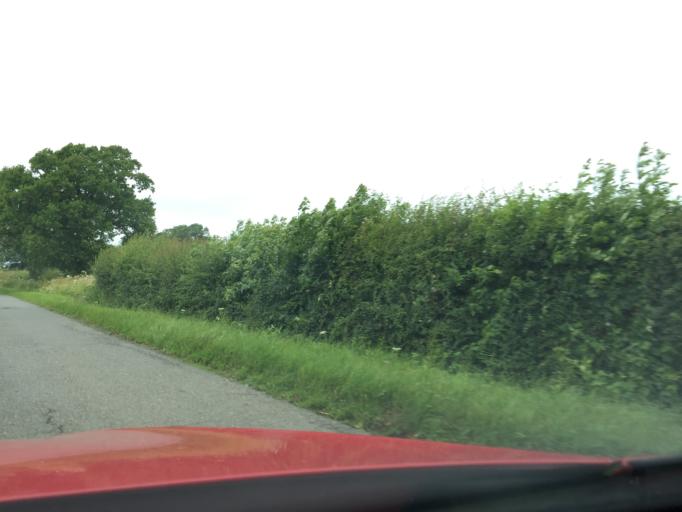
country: GB
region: England
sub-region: Northamptonshire
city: Daventry
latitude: 52.2413
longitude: -1.1842
